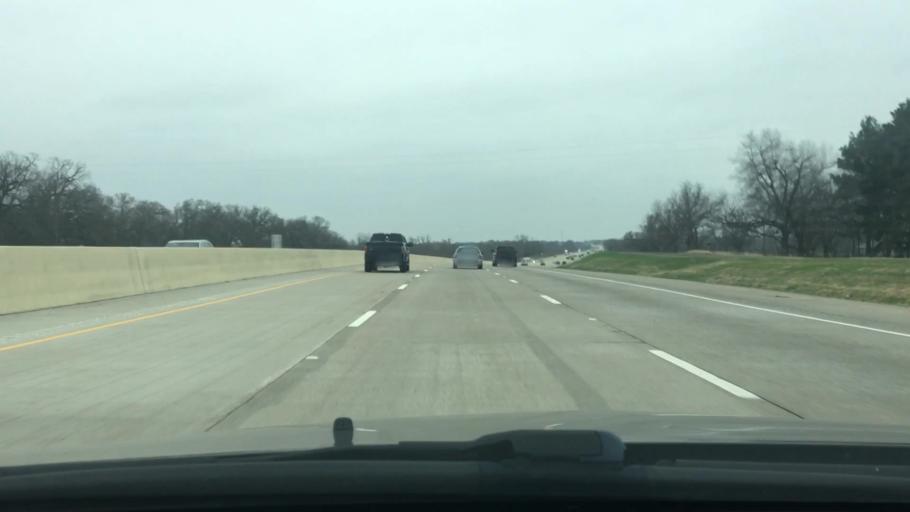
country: US
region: Texas
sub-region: Navarro County
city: Corsicana
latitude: 31.9581
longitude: -96.4205
